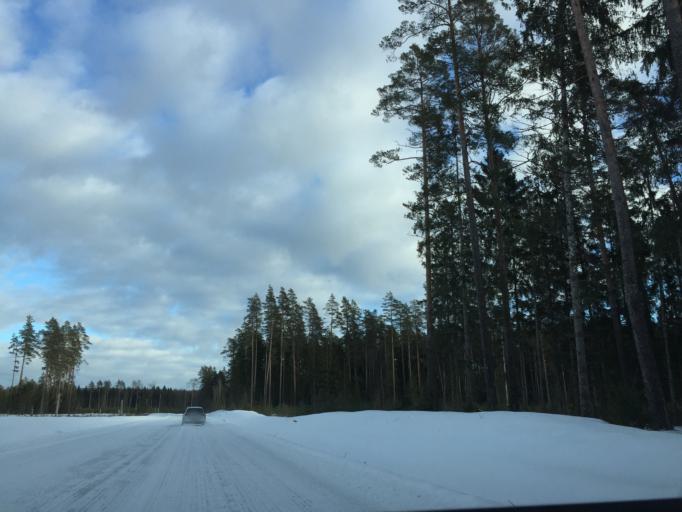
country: LV
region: Ogre
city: Jumprava
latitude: 56.5490
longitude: 24.8794
